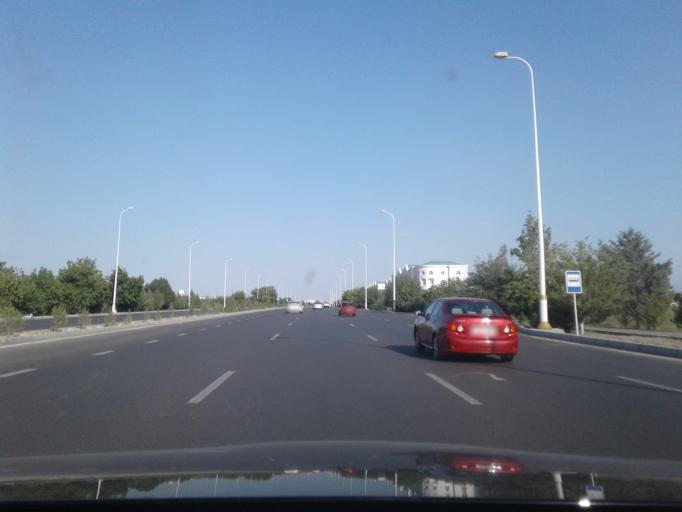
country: TM
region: Ahal
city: Ashgabat
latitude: 37.9953
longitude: 58.3097
